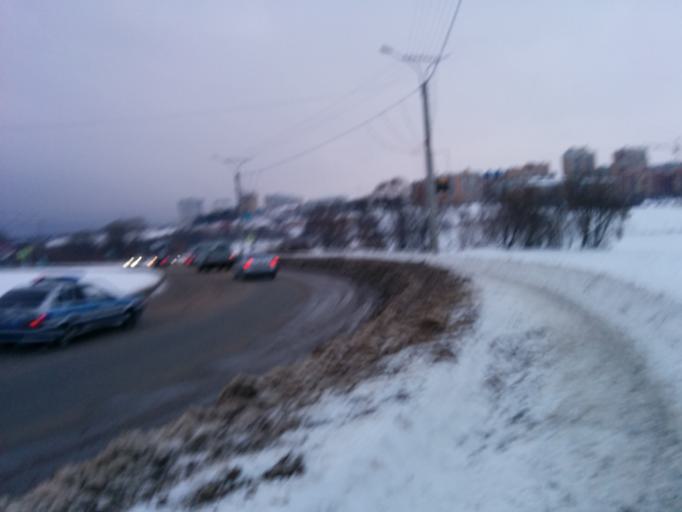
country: RU
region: Chuvashia
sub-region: Cheboksarskiy Rayon
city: Cheboksary
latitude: 56.1369
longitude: 47.2373
